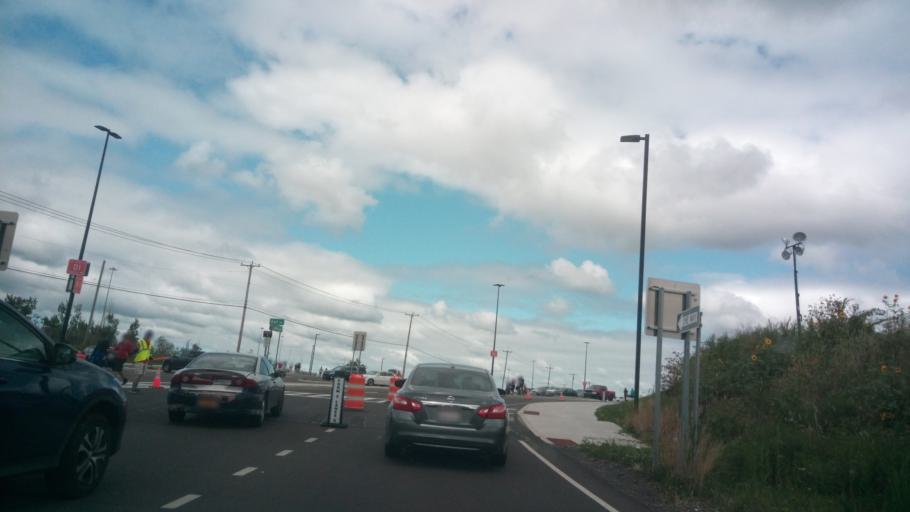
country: US
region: New York
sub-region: Onondaga County
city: Solvay
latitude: 43.0780
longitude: -76.2137
